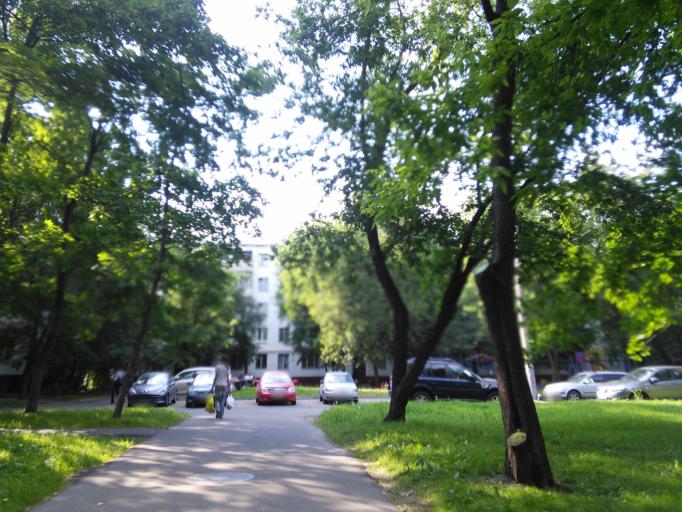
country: RU
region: Moskovskaya
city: Bogorodskoye
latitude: 55.8099
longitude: 37.7238
